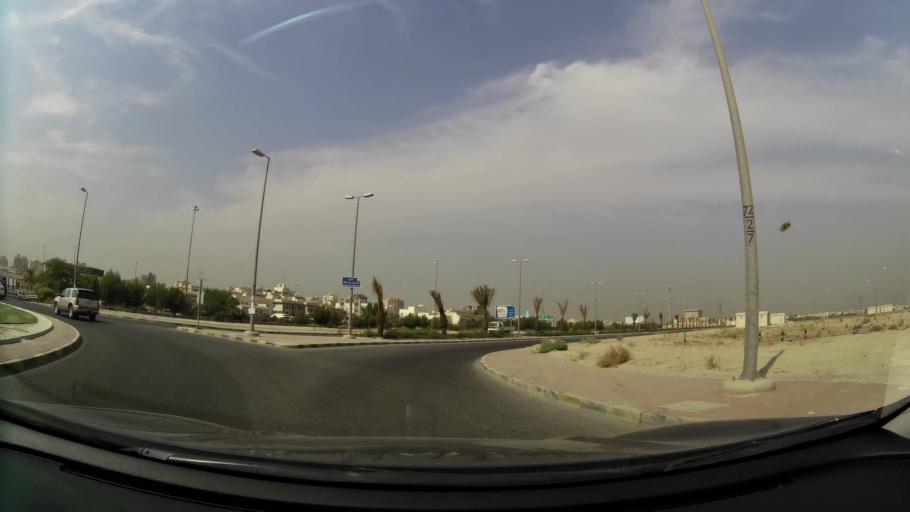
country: KW
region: Al Farwaniyah
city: Janub as Surrah
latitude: 29.2941
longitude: 47.9833
